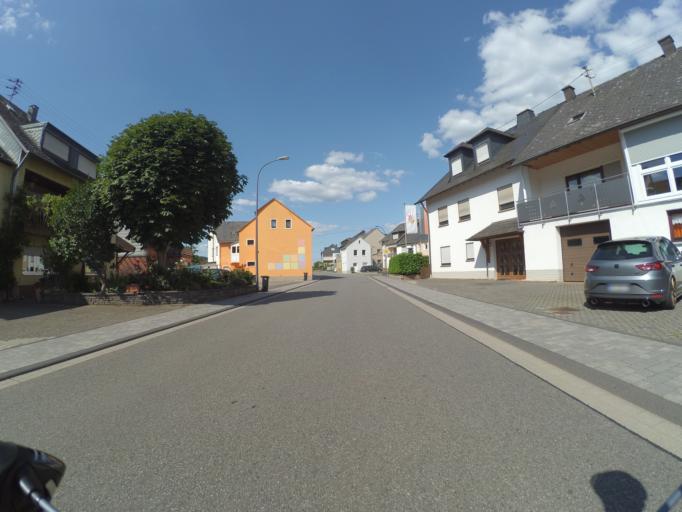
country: DE
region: Rheinland-Pfalz
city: Fell
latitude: 49.7726
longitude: 6.7817
